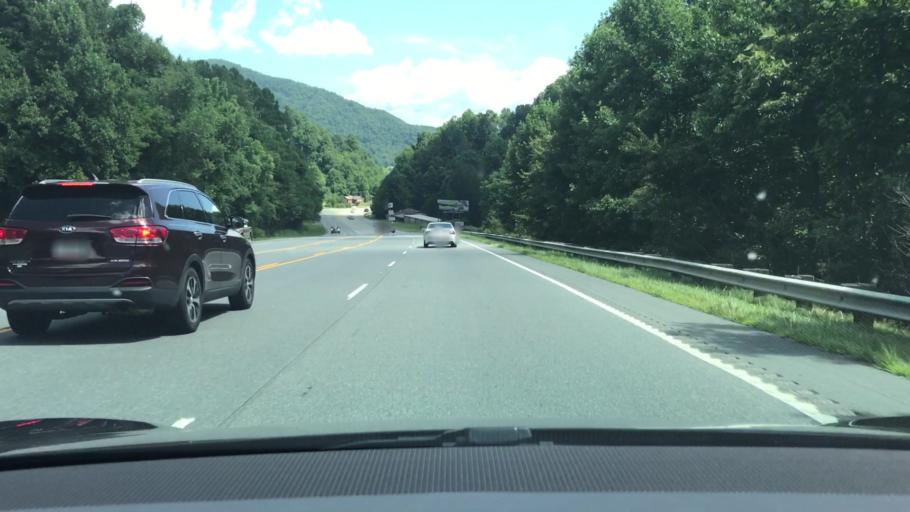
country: US
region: North Carolina
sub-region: Jackson County
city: Sylva
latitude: 35.2747
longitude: -83.2899
